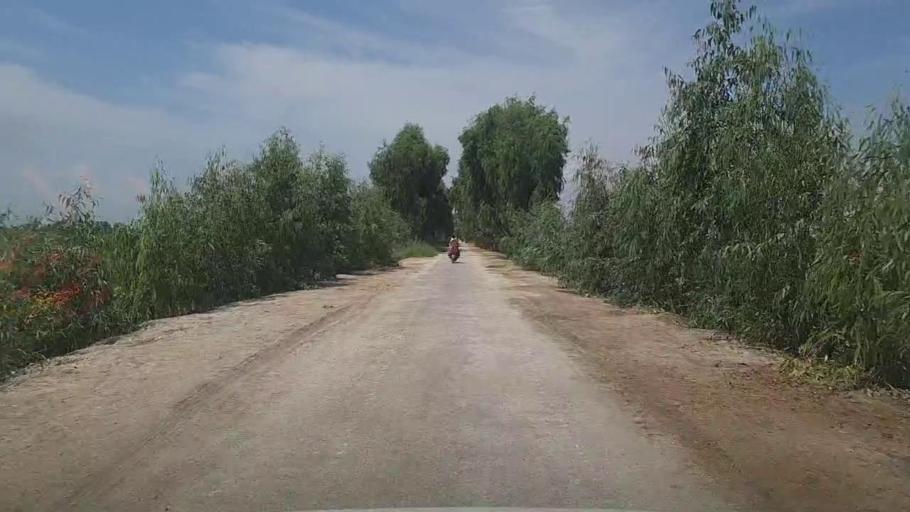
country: PK
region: Sindh
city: Kandhkot
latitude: 28.2905
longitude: 69.2386
